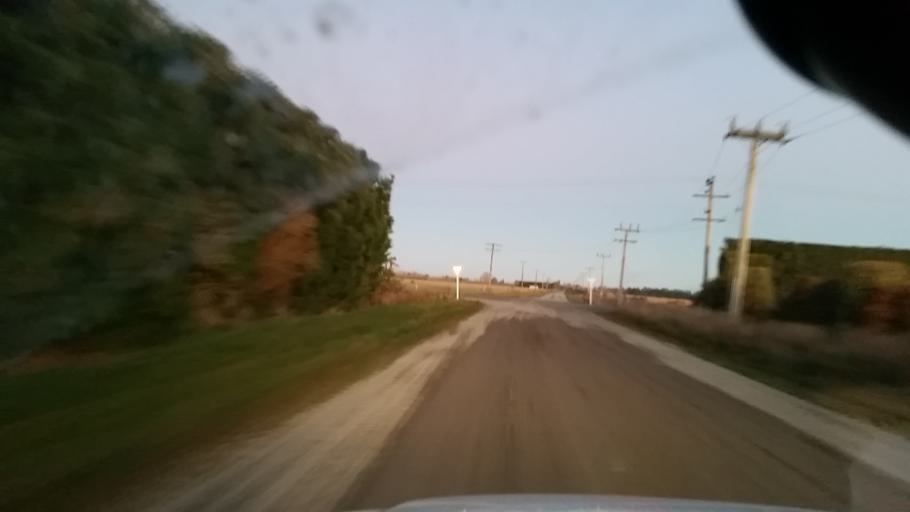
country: NZ
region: Canterbury
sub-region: Ashburton District
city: Tinwald
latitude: -43.9908
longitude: 171.6577
